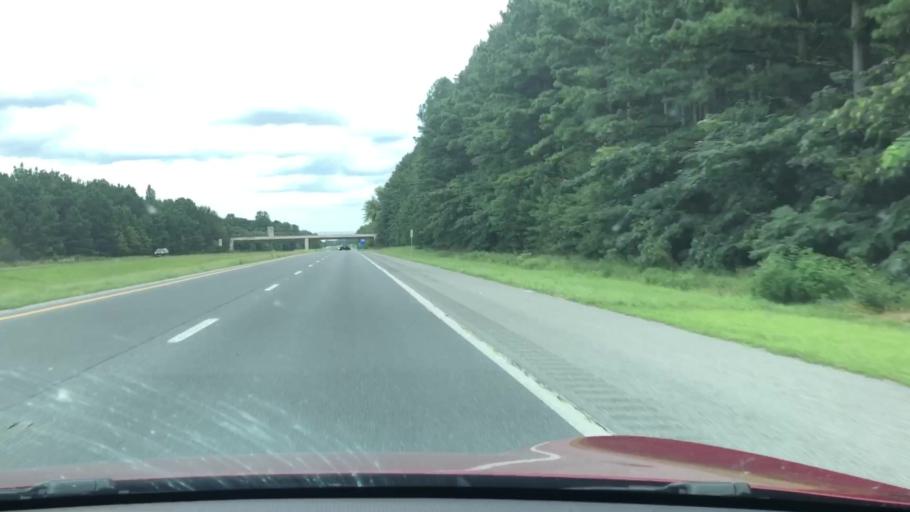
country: US
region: Maryland
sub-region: Wicomico County
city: Fruitland
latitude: 38.3185
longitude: -75.5884
